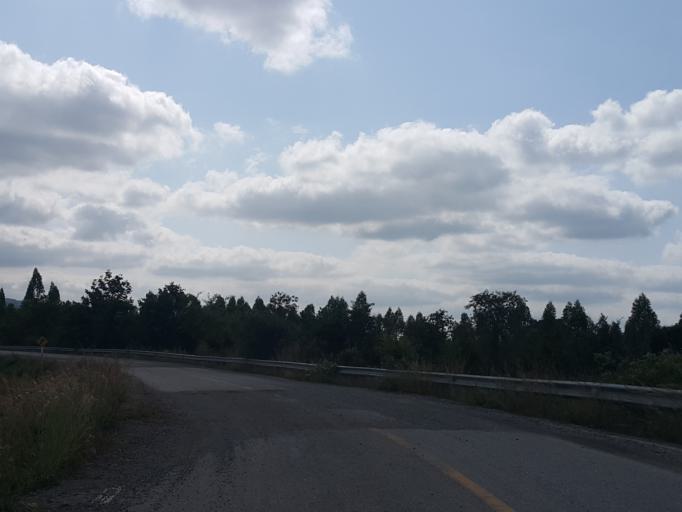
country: TH
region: Lamphun
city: Mae Tha
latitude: 18.5364
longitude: 99.0863
